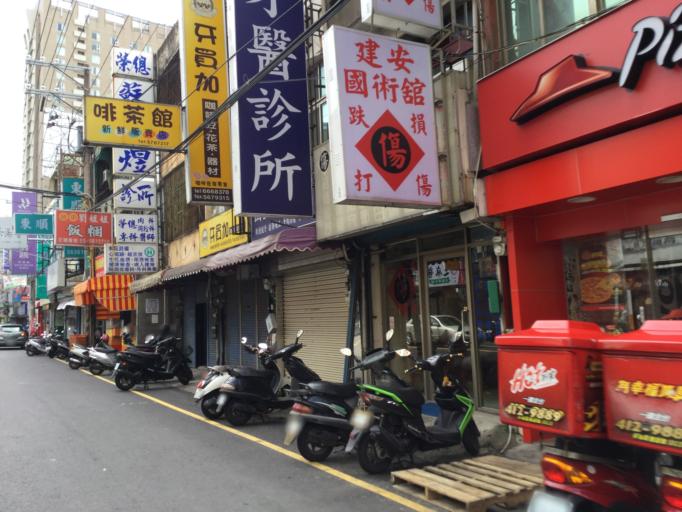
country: TW
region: Taiwan
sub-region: Hsinchu
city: Hsinchu
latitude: 24.7827
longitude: 121.0189
